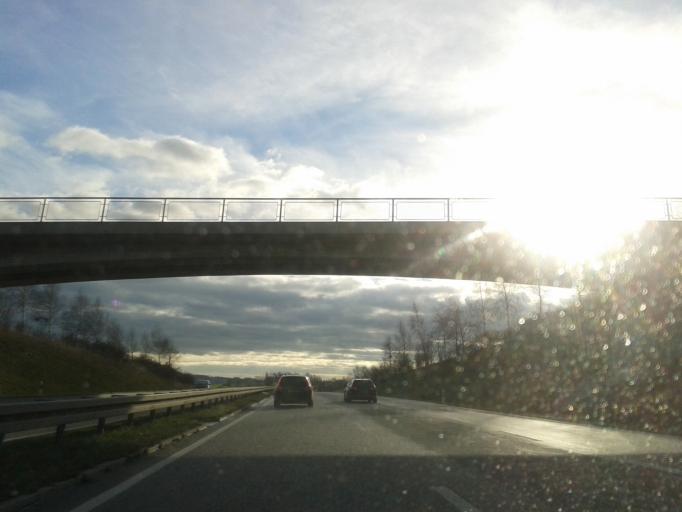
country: DE
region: Saxony
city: Grossschweidnitz
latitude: 51.0917
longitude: 14.6411
